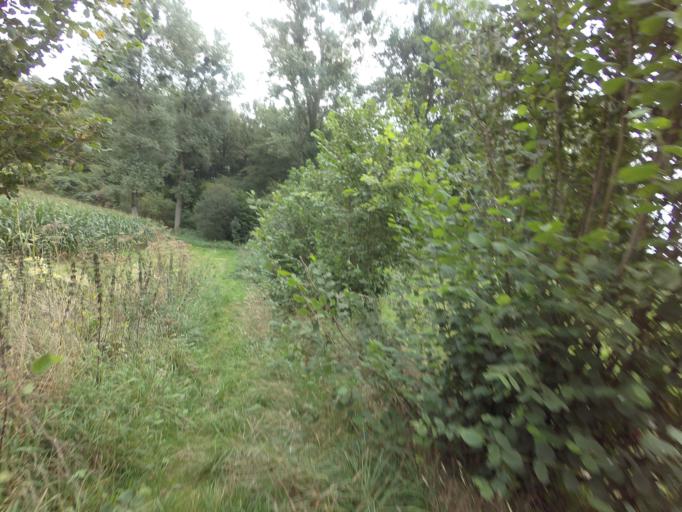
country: NL
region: Limburg
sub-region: Gemeente Simpelveld
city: Simpelveld
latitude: 50.8022
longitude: 5.9834
